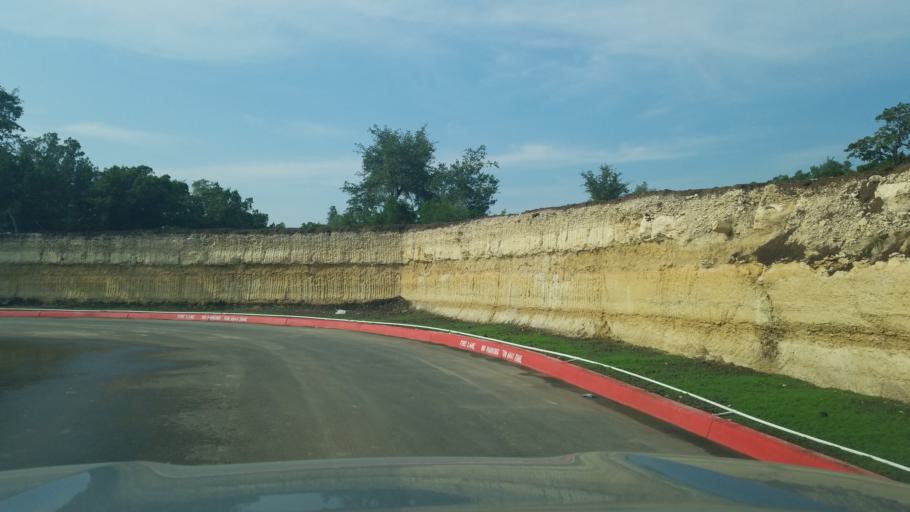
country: US
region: Texas
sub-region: Bexar County
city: Timberwood Park
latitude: 29.7162
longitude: -98.4705
